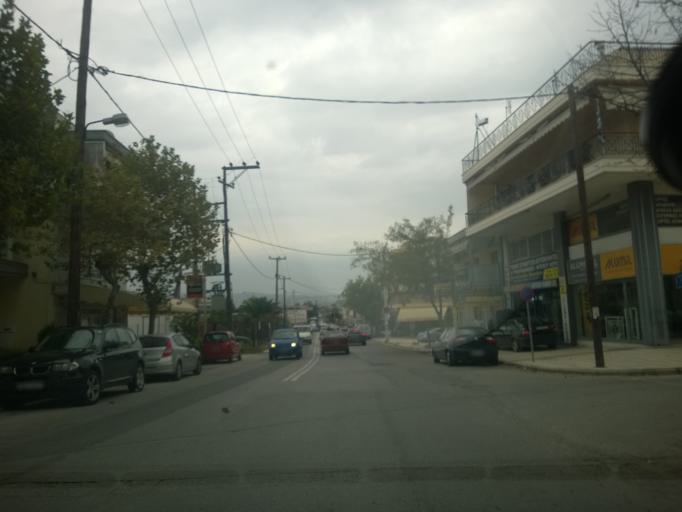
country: GR
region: Central Macedonia
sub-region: Nomos Thessalonikis
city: Stavroupoli
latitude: 40.6762
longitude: 22.9361
